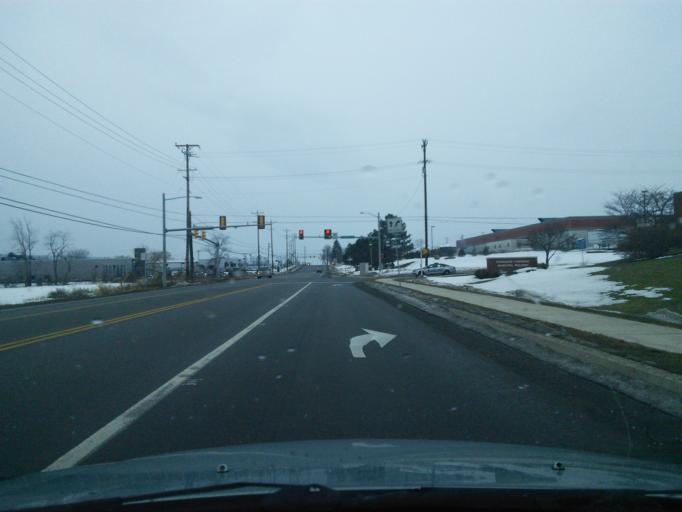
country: US
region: Pennsylvania
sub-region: Centre County
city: Pine Grove Mills
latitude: 40.7624
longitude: -77.8750
